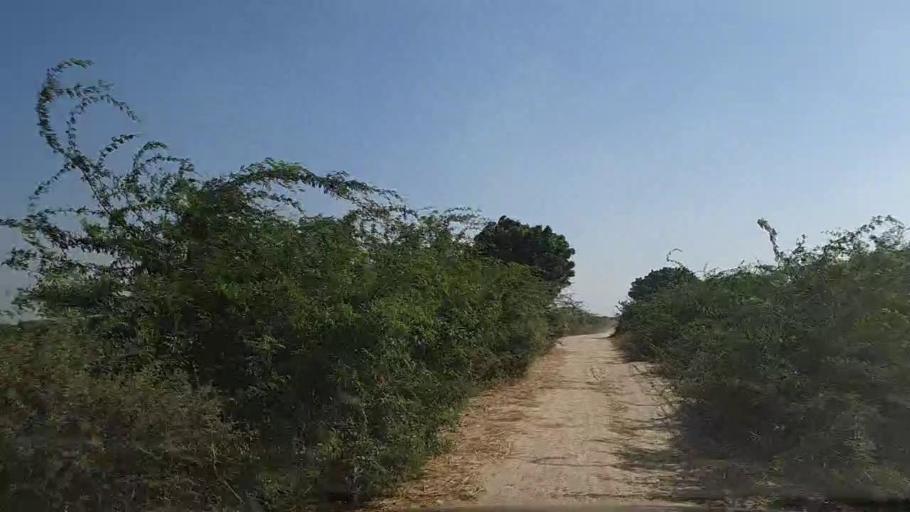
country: PK
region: Sindh
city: Daro Mehar
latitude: 24.8137
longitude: 68.0738
